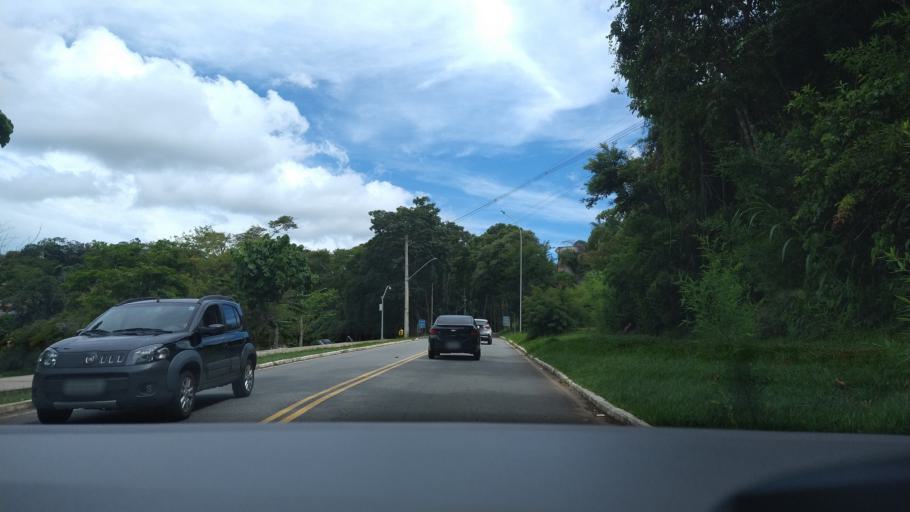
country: BR
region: Minas Gerais
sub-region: Vicosa
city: Vicosa
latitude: -20.7632
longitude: -42.8708
